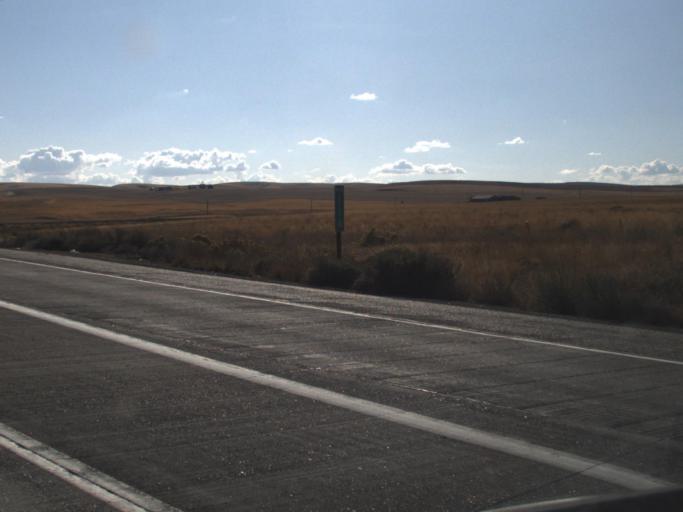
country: US
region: Washington
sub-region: Benton County
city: Highland
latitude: 46.1465
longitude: -119.2022
